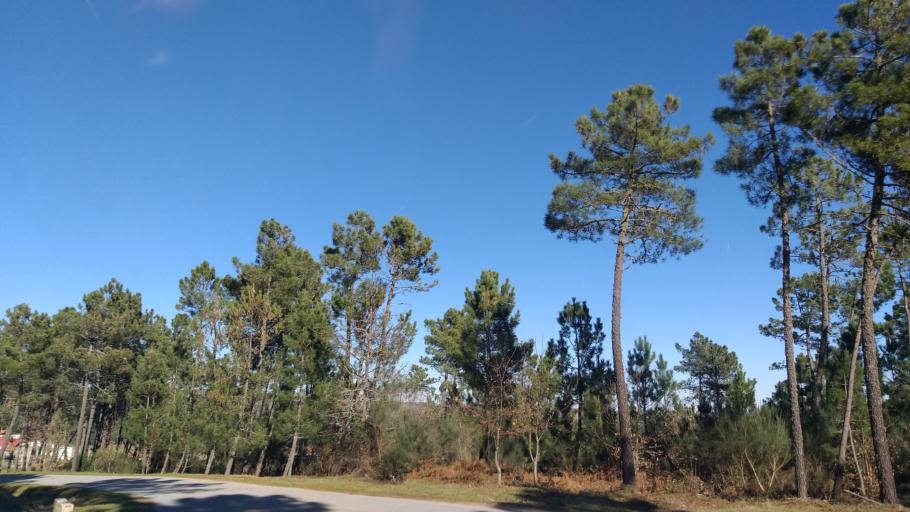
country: PT
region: Guarda
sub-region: Celorico da Beira
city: Celorico da Beira
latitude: 40.5147
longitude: -7.4045
